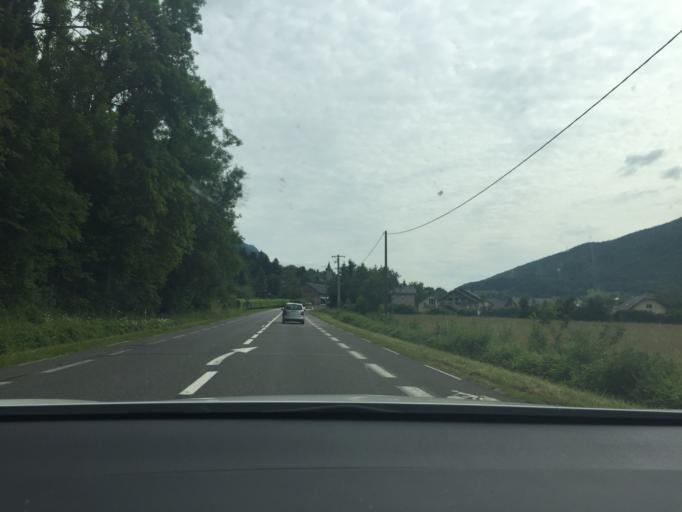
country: FR
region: Rhone-Alpes
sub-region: Departement de la Savoie
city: Vimines
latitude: 45.5059
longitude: 5.8484
